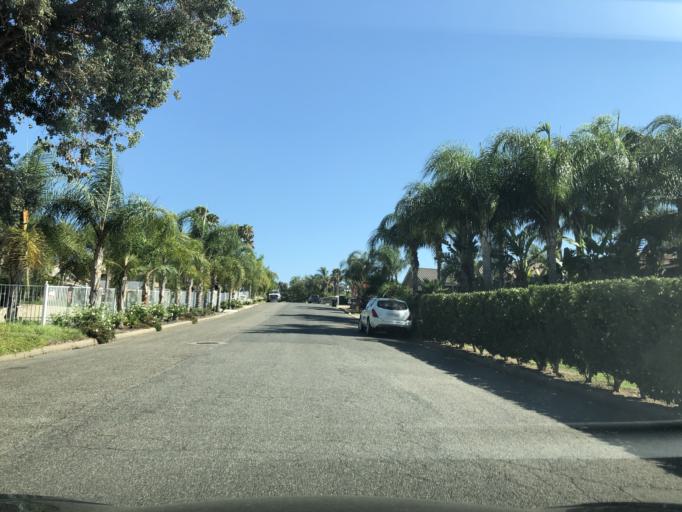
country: US
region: California
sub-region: Riverside County
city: El Cerrito
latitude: 33.8574
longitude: -117.5346
